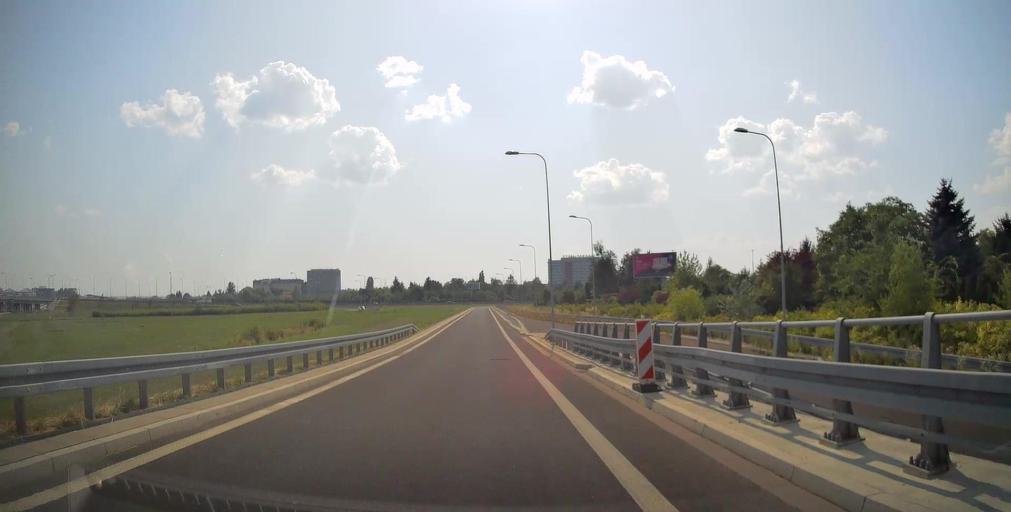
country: PL
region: Masovian Voivodeship
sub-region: Warszawa
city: Ochota
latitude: 52.1844
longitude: 20.9861
